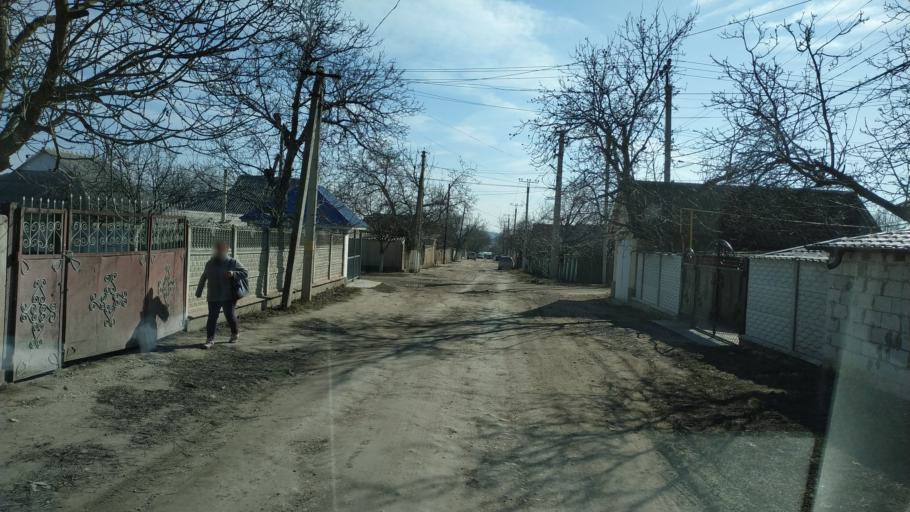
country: MD
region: Nisporeni
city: Nisporeni
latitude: 47.0785
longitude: 28.1624
